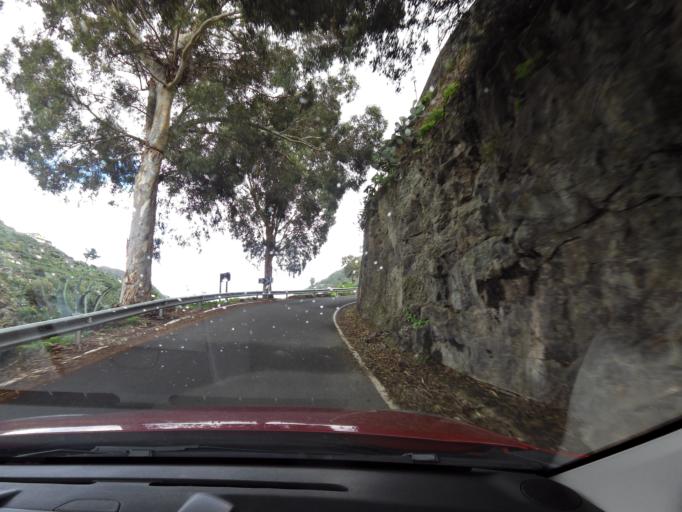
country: ES
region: Canary Islands
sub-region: Provincia de Las Palmas
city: Santa Brigida
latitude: 28.0222
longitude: -15.4761
